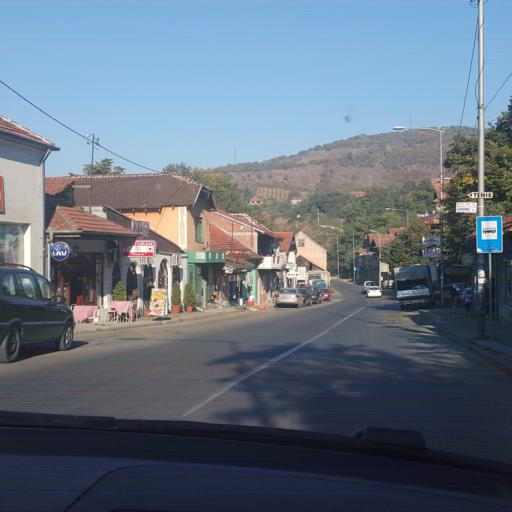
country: RS
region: Central Serbia
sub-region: Toplicki Okrug
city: Prokuplje
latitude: 43.2319
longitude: 21.5823
